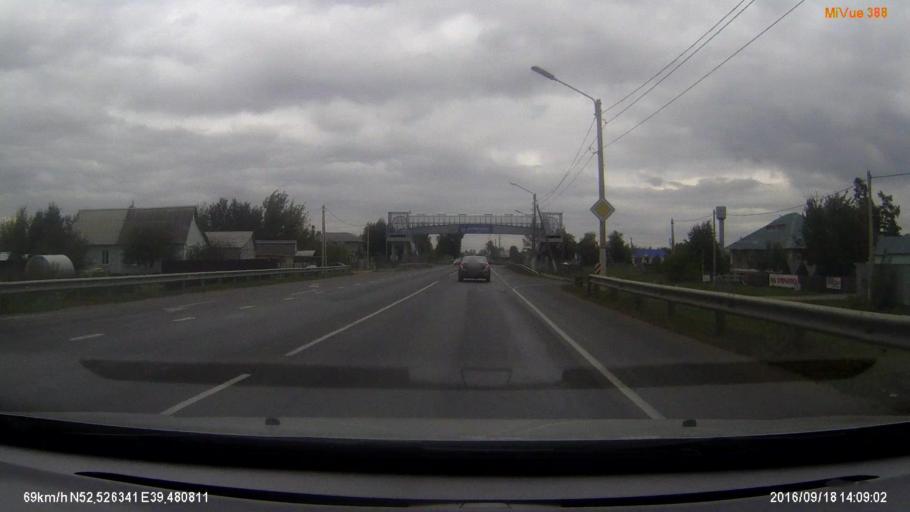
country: RU
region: Lipetsk
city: Syrskoye
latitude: 52.5909
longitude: 39.5260
